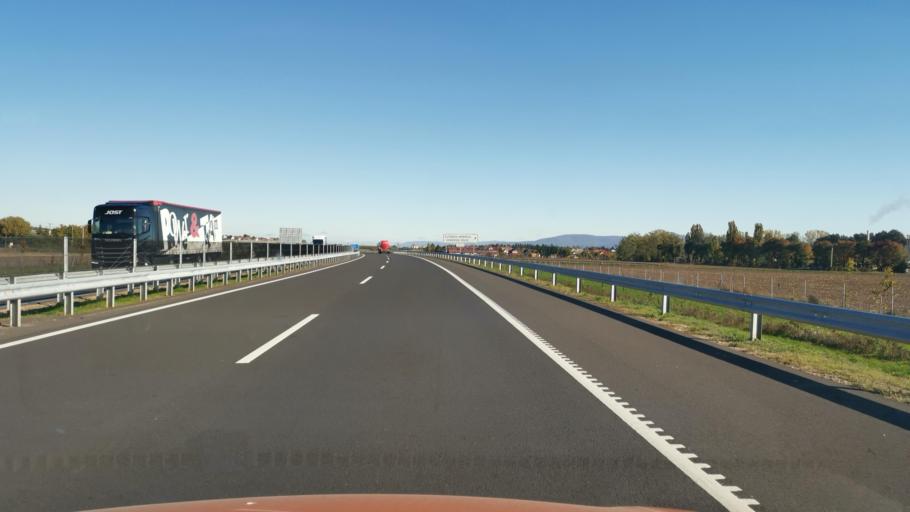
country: HU
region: Borsod-Abauj-Zemplen
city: Encs
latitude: 48.3239
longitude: 21.0978
